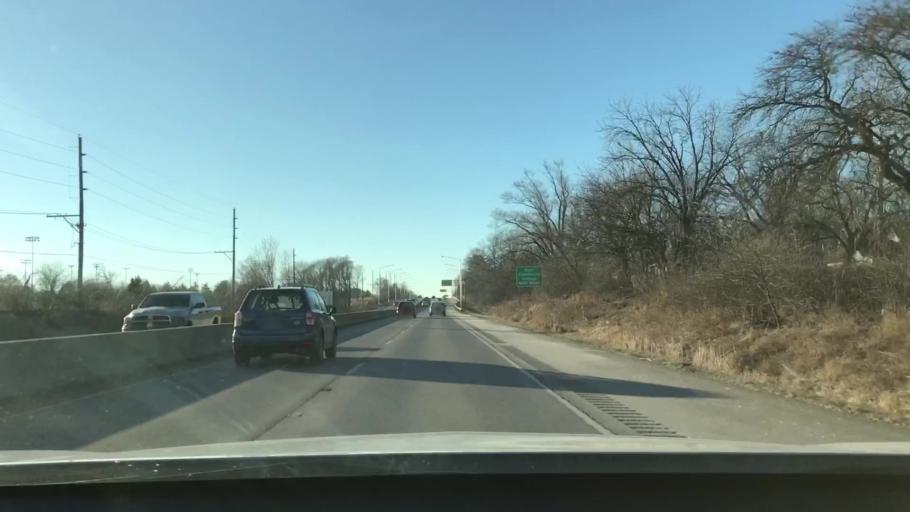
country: US
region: Illinois
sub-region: Kane County
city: Elgin
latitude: 42.0228
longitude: -88.2941
